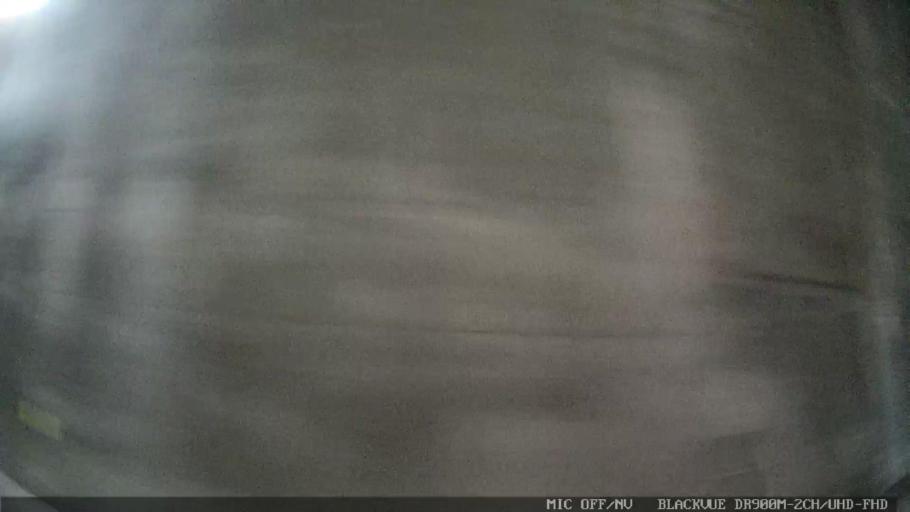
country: BR
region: Sao Paulo
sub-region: Cubatao
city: Cubatao
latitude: -23.9127
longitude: -46.5275
